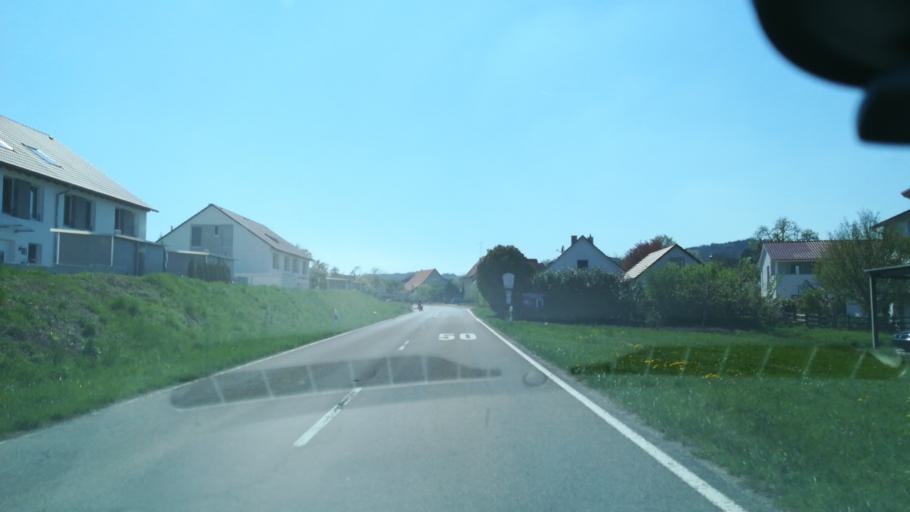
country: DE
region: Baden-Wuerttemberg
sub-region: Freiburg Region
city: Volkertshausen
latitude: 47.7945
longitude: 8.8425
